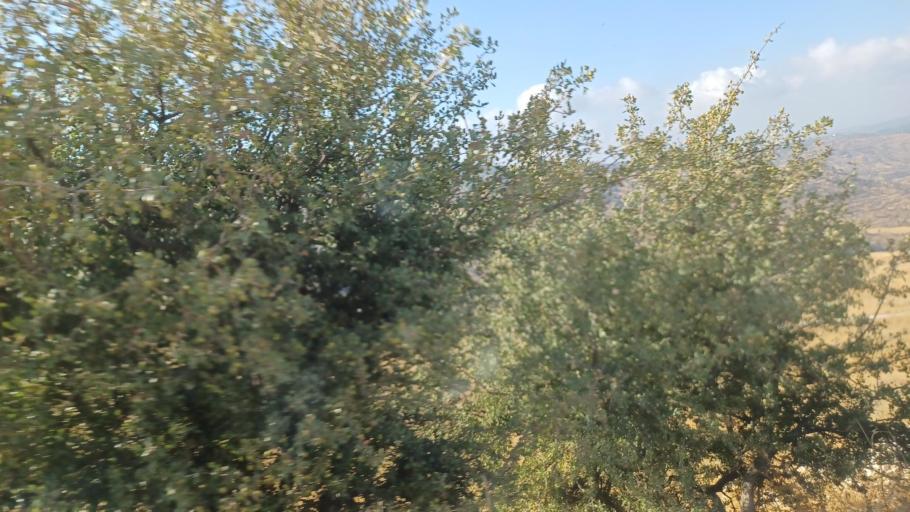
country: CY
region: Pafos
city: Mesogi
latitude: 34.8729
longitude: 32.6120
